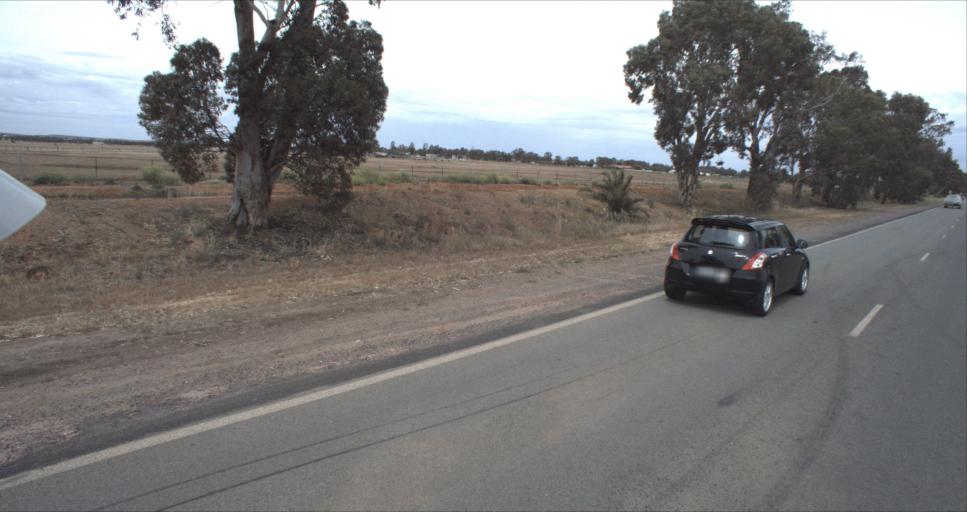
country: AU
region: New South Wales
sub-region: Leeton
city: Leeton
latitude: -34.5299
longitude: 146.4097
